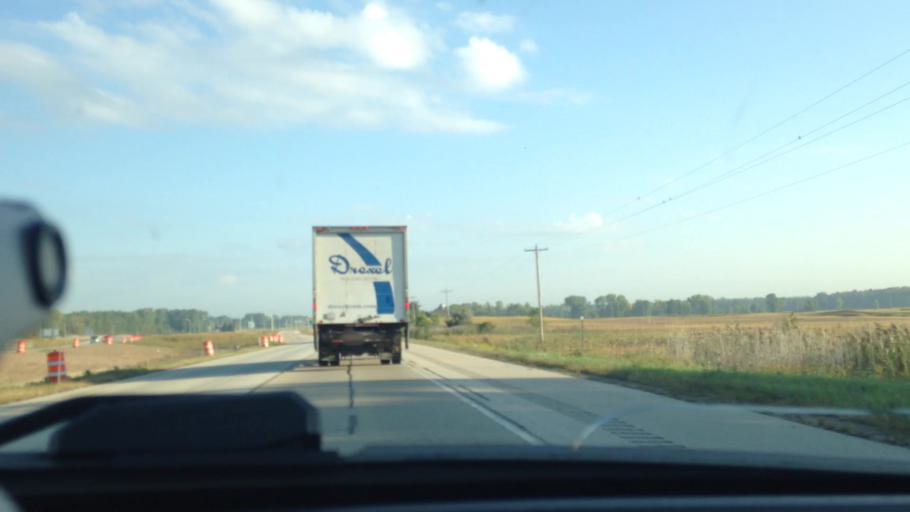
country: US
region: Wisconsin
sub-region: Brown County
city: Suamico
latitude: 44.7355
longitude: -88.0506
